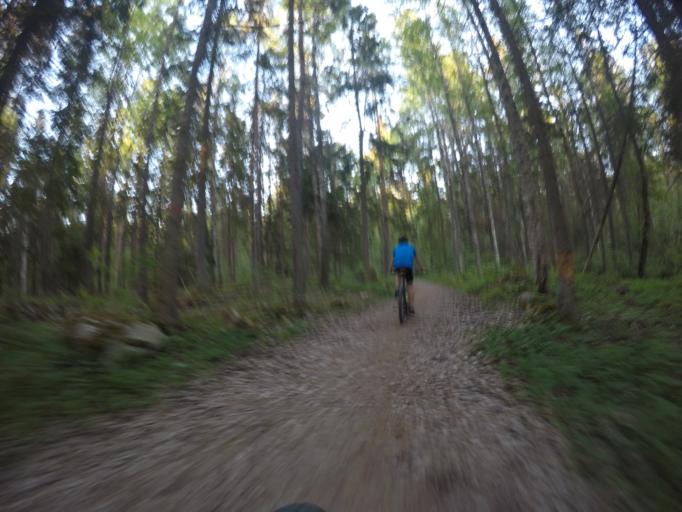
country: SE
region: Soedermanland
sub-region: Eskilstuna Kommun
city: Skogstorp
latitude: 59.3403
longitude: 16.4985
